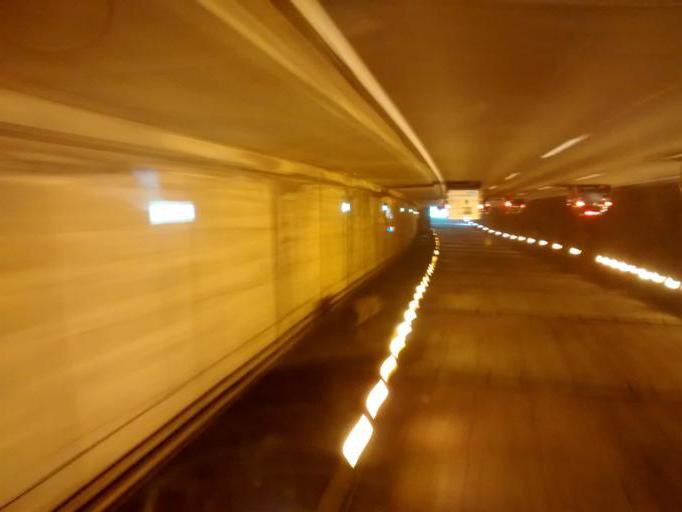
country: ES
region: Catalonia
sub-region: Provincia de Barcelona
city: Nou Barris
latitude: 41.4456
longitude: 2.1774
